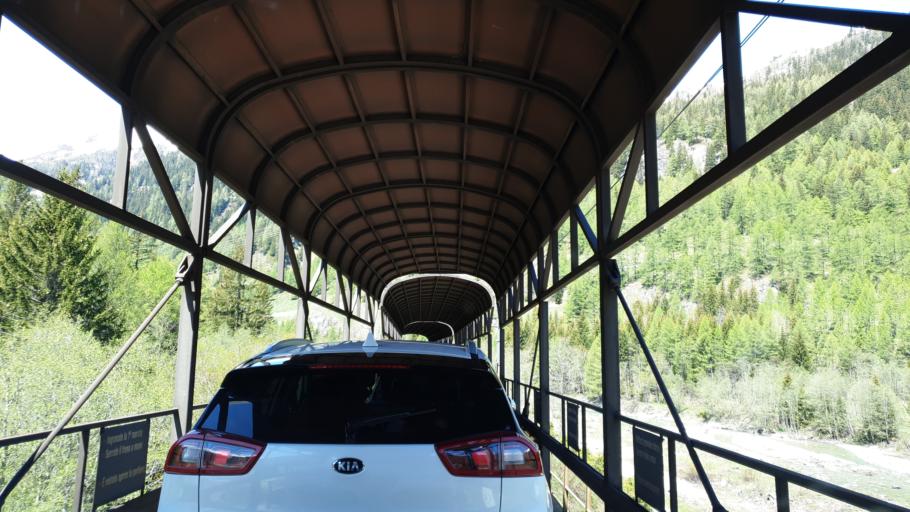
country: IT
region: Piedmont
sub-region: Provincia Verbano-Cusio-Ossola
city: Formazza
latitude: 46.5362
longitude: 8.3572
